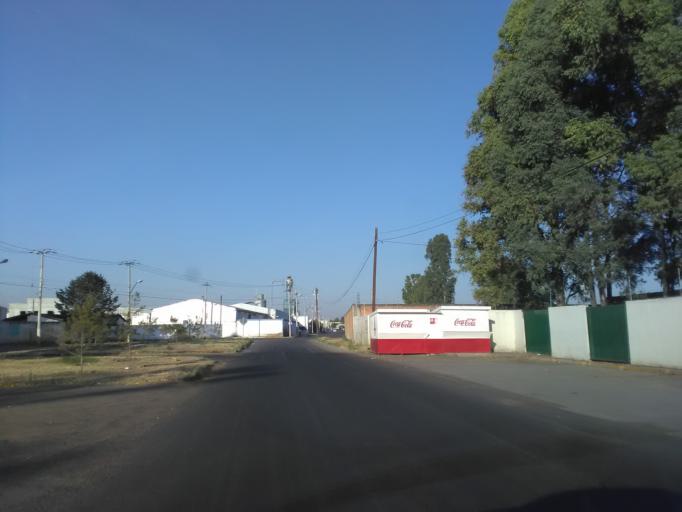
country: MX
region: Durango
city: Victoria de Durango
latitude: 24.0641
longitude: -104.6102
